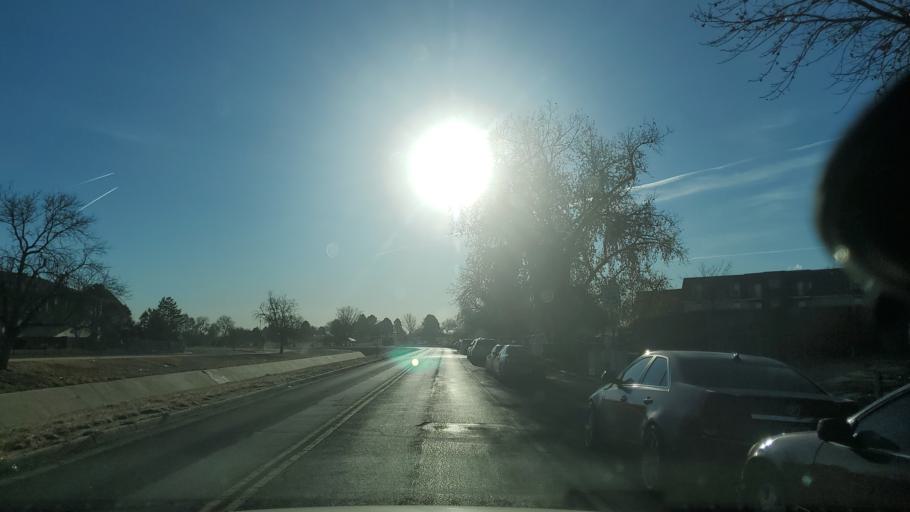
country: US
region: Colorado
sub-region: Adams County
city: Welby
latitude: 39.8430
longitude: -104.9687
